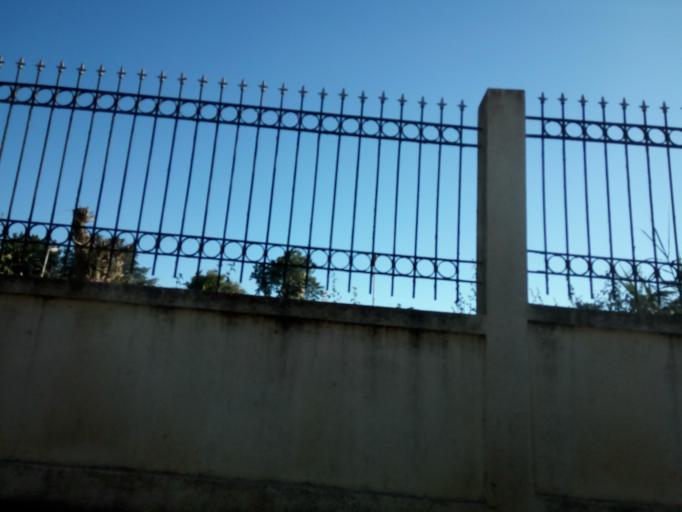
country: DZ
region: Tipaza
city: Saoula
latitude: 36.7268
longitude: 3.0080
